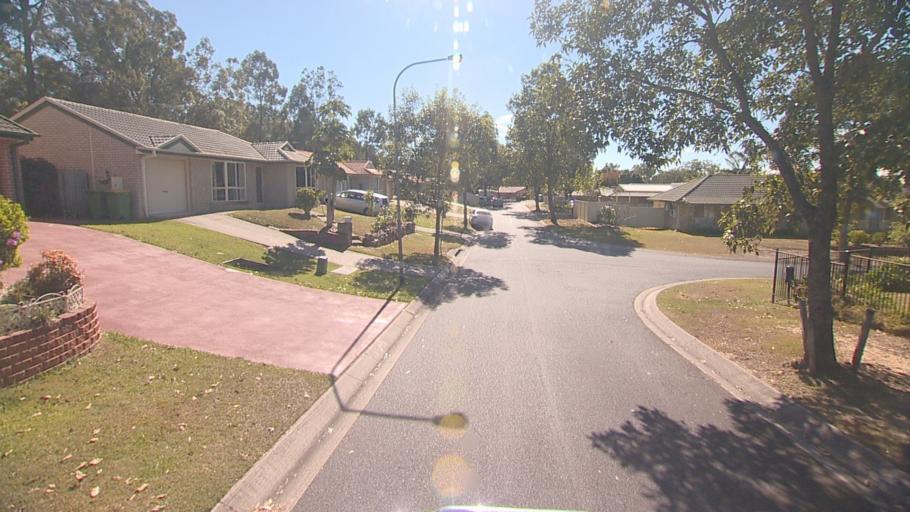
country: AU
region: Queensland
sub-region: Logan
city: Park Ridge South
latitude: -27.6749
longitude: 153.0190
